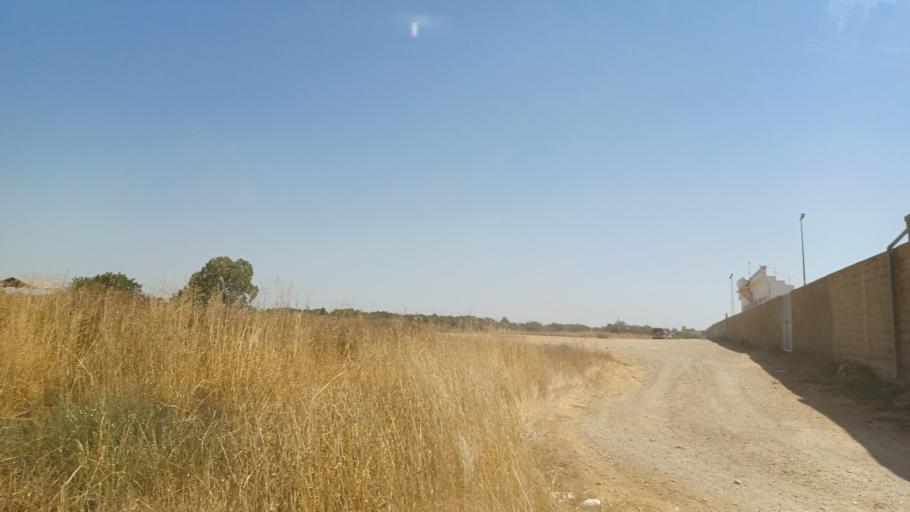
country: CY
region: Ammochostos
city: Avgorou
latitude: 35.0204
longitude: 33.8271
